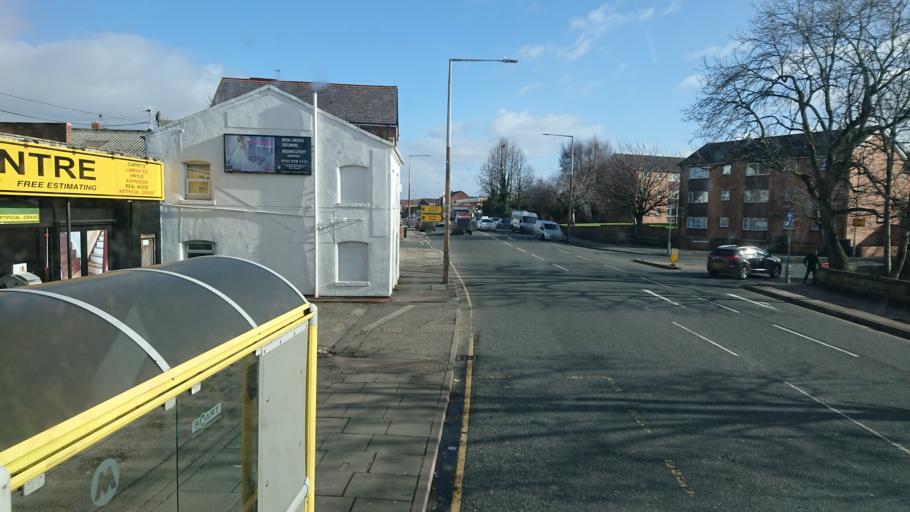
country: GB
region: England
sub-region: Metropolitan Borough of Wirral
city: Moreton
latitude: 53.4013
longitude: -3.1101
